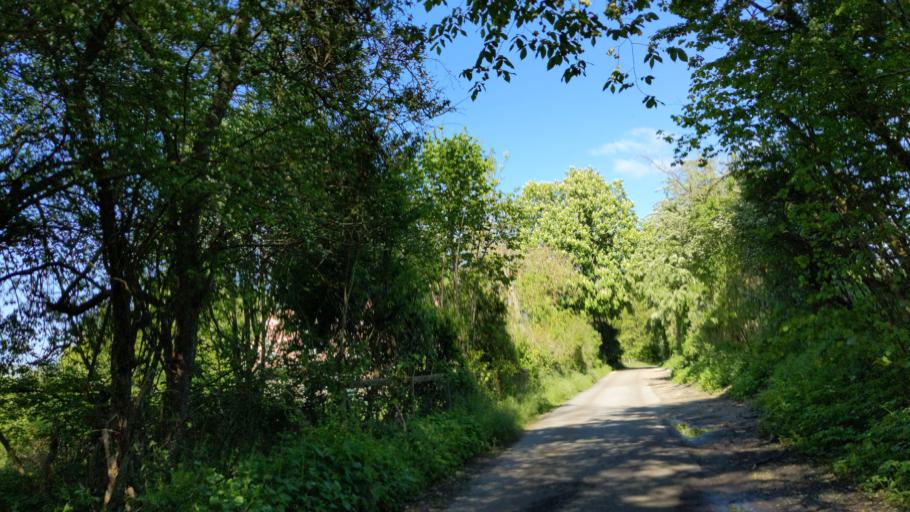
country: DE
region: Schleswig-Holstein
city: Eutin
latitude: 54.1038
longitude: 10.5897
